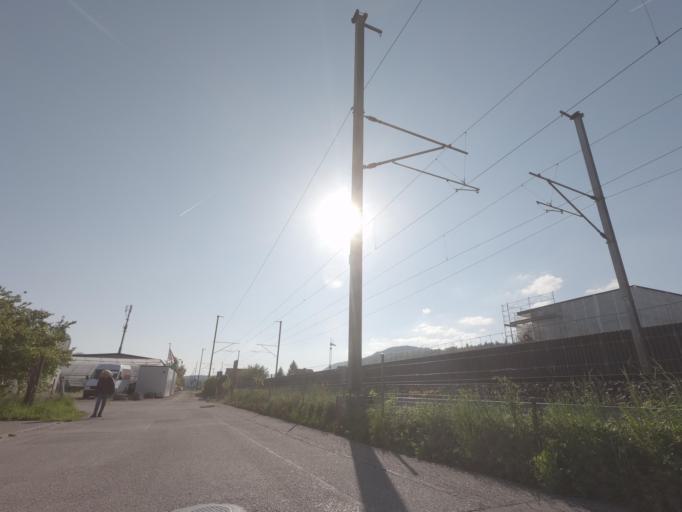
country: CH
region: Bern
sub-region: Biel/Bienne District
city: Lengnau
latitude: 47.1844
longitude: 7.3784
